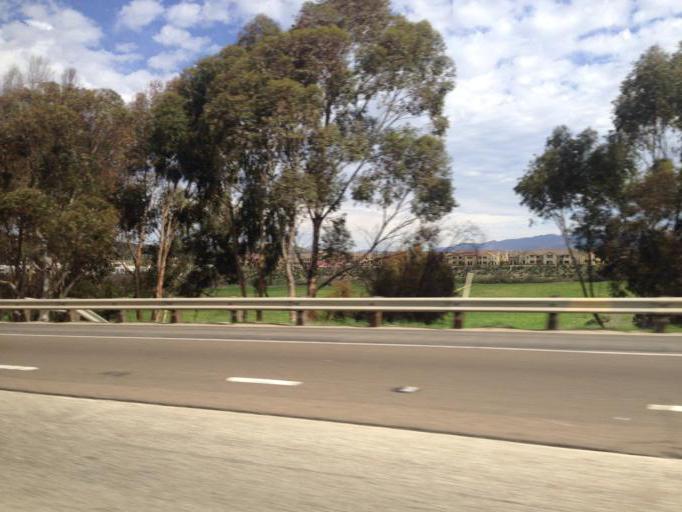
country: US
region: California
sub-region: San Diego County
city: Bonita
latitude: 32.5881
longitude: -117.0362
